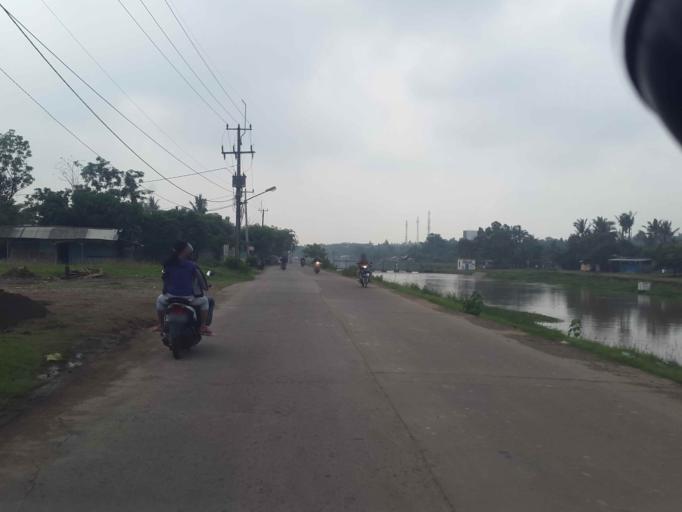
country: ID
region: West Java
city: Cikarang
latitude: -6.3411
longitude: 107.1987
